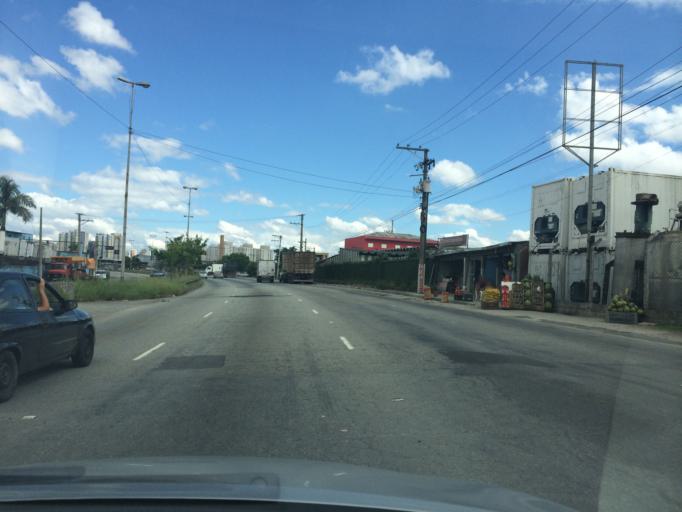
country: BR
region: Sao Paulo
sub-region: Guarulhos
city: Guarulhos
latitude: -23.5163
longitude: -46.5616
